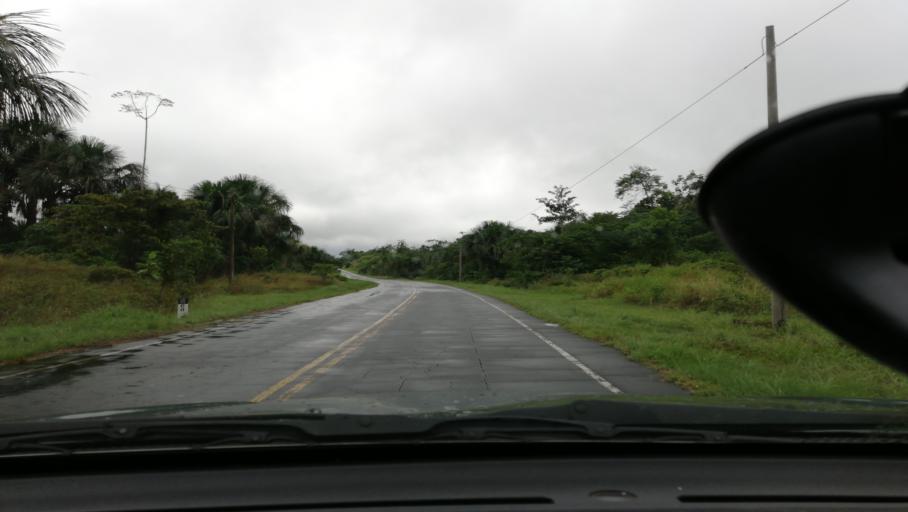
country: PE
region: Loreto
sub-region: Provincia de Loreto
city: Nauta
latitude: -4.2513
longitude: -73.4959
